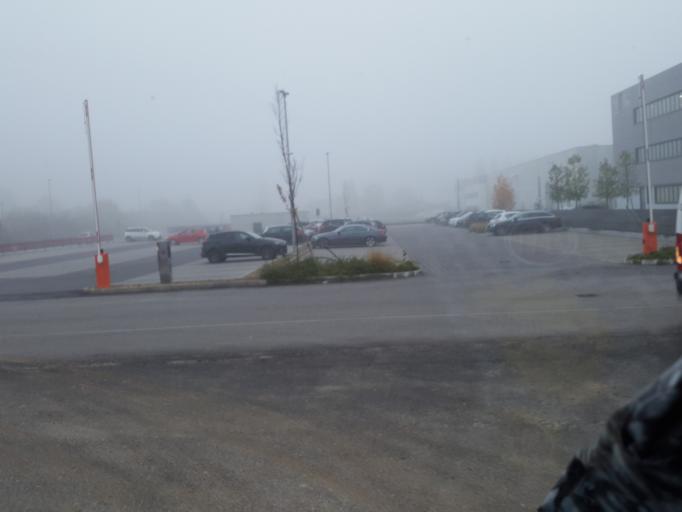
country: IT
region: Veneto
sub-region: Provincia di Padova
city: Borgoricco-San Michele delle Badesse-Sant'Eufemia
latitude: 45.5398
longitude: 11.9504
